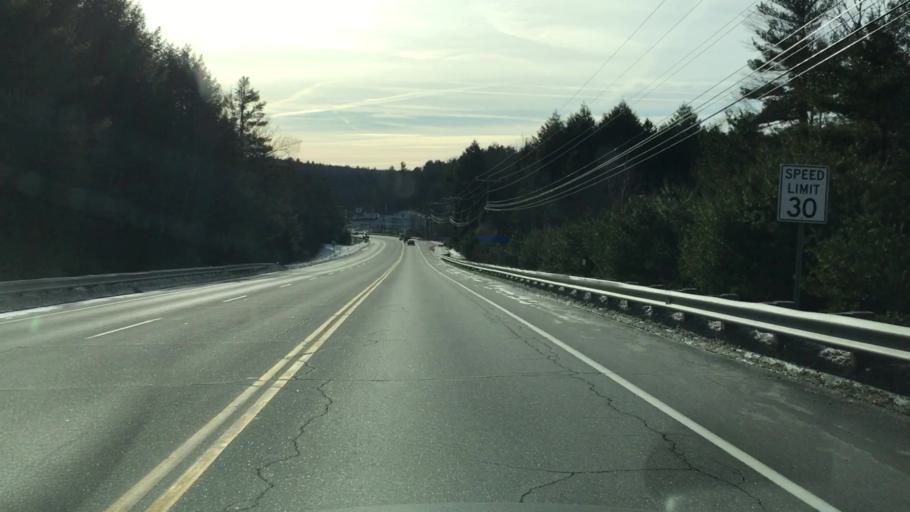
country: US
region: New Hampshire
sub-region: Sullivan County
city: Sunapee
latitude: 43.3953
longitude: -72.0853
